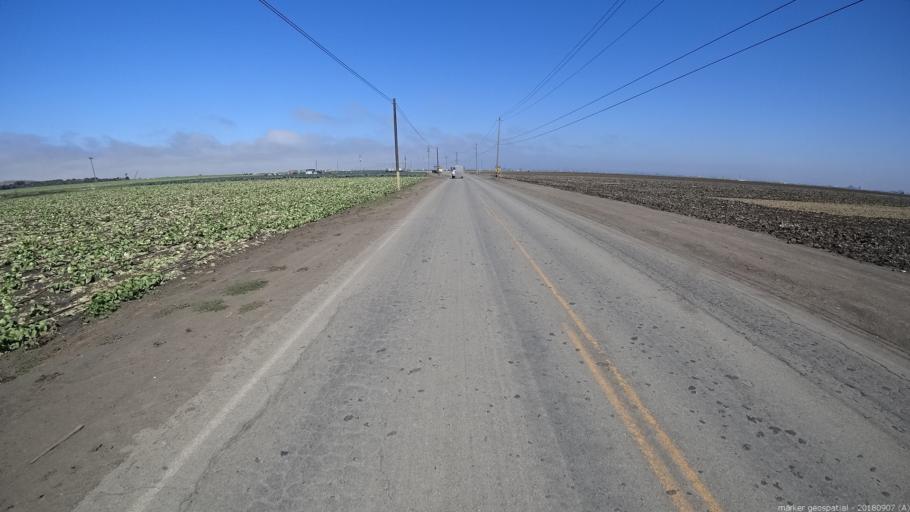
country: US
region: California
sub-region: Monterey County
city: Boronda
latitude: 36.6993
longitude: -121.7349
